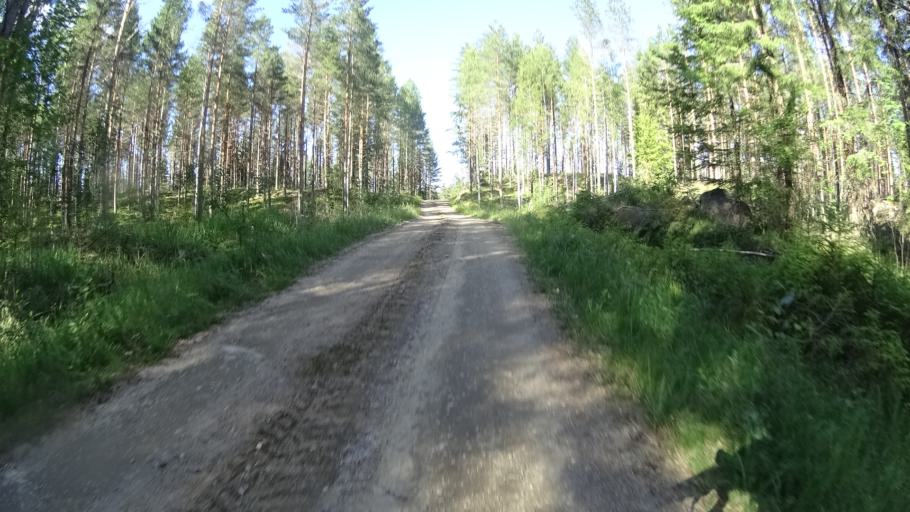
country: FI
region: Uusimaa
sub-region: Helsinki
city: Karkkila
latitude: 60.6399
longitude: 24.1623
